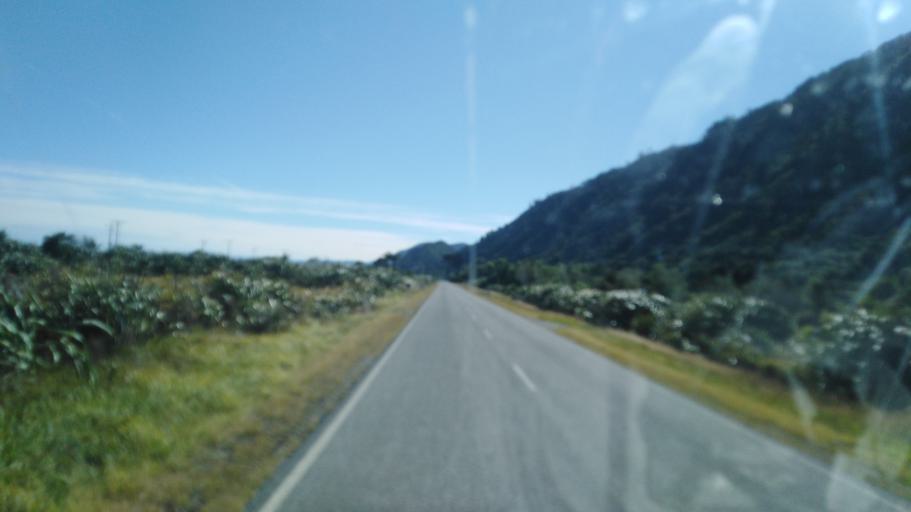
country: NZ
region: West Coast
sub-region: Buller District
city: Westport
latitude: -41.6434
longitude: 171.8405
